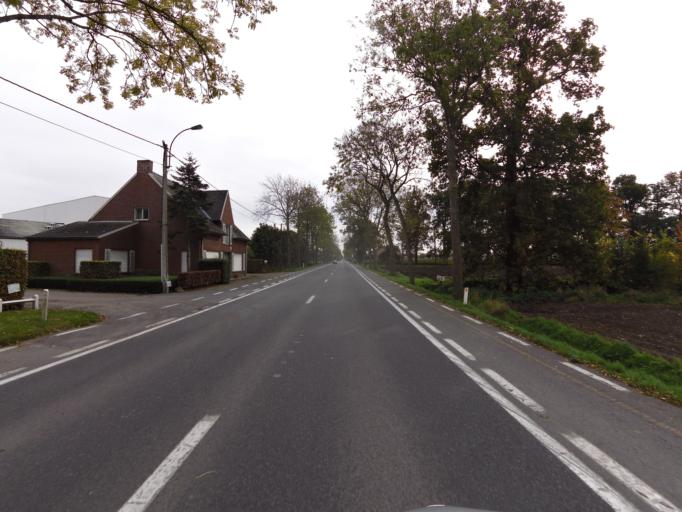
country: BE
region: Flanders
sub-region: Provincie West-Vlaanderen
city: Ichtegem
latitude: 51.1137
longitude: 3.0120
